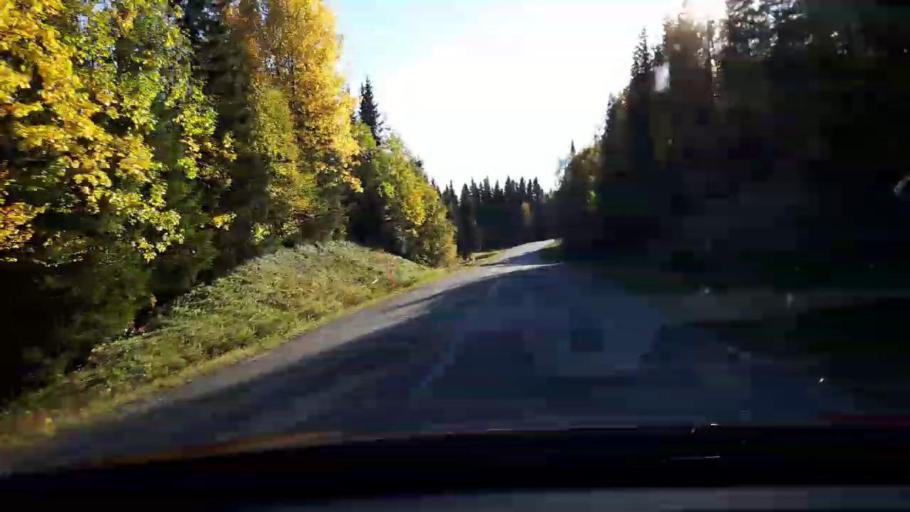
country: SE
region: Jaemtland
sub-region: OEstersunds Kommun
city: Lit
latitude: 63.8286
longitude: 14.8683
